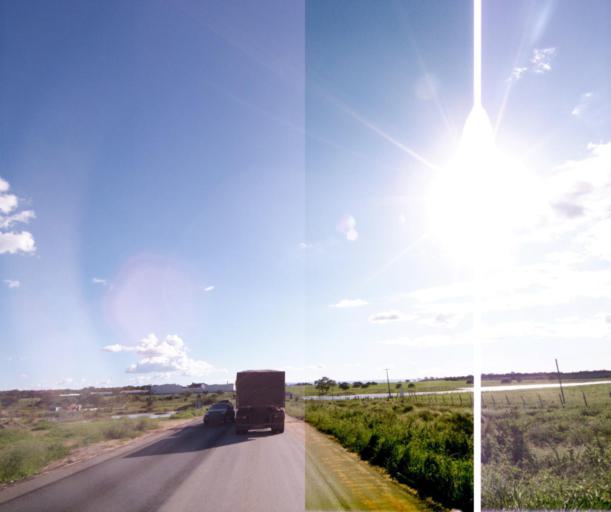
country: BR
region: Bahia
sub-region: Guanambi
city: Guanambi
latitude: -14.1845
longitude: -42.7378
